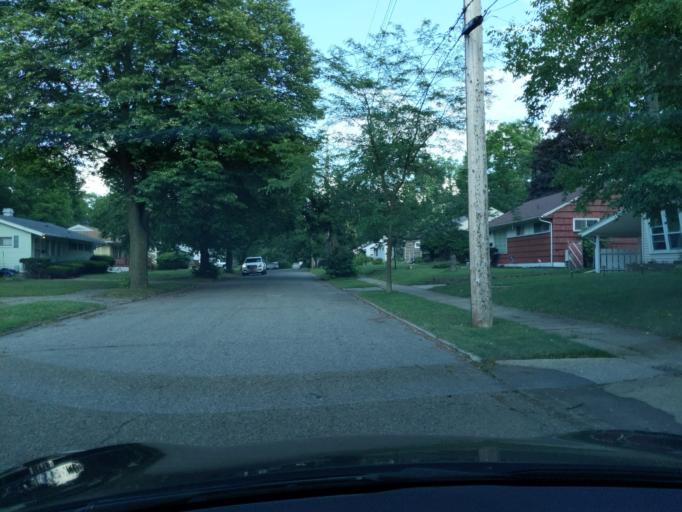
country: US
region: Michigan
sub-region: Ingham County
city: Lansing
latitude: 42.6894
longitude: -84.5527
